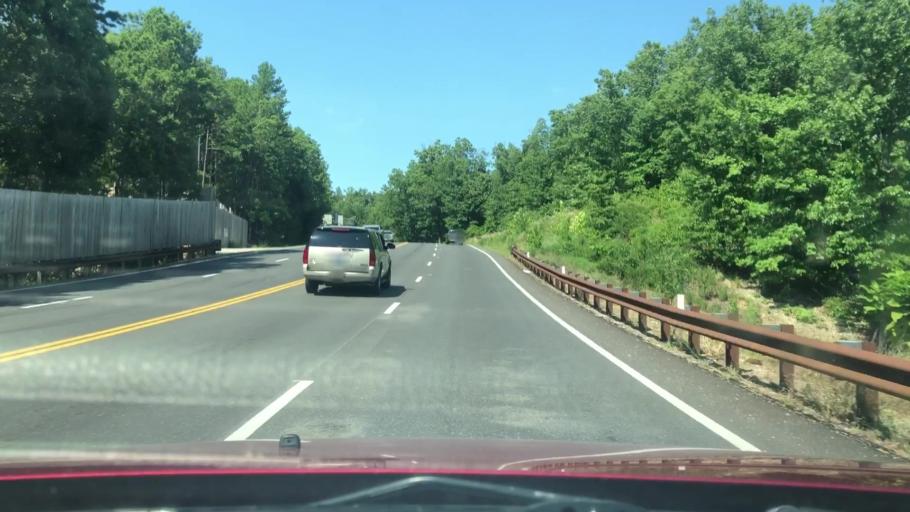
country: US
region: Missouri
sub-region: Stone County
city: Kimberling City
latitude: 36.6683
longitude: -93.3361
